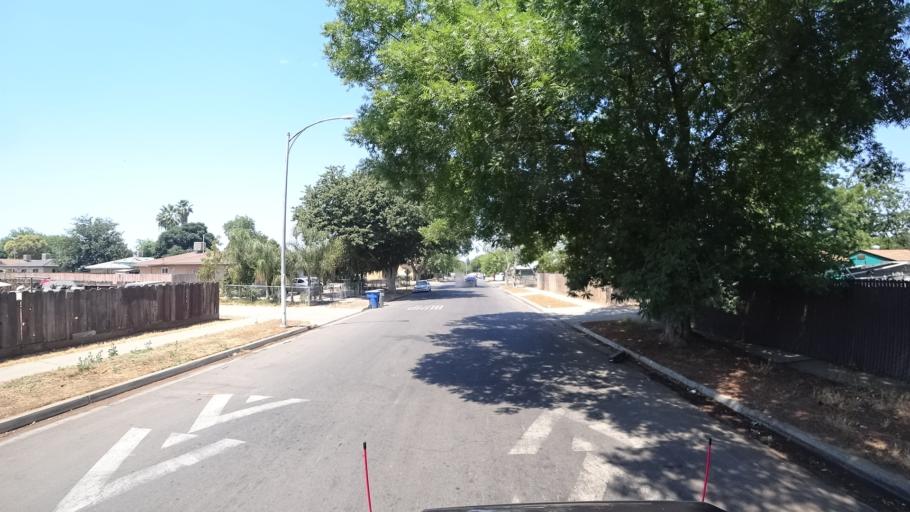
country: US
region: California
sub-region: Fresno County
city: Fresno
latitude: 36.7160
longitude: -119.7968
